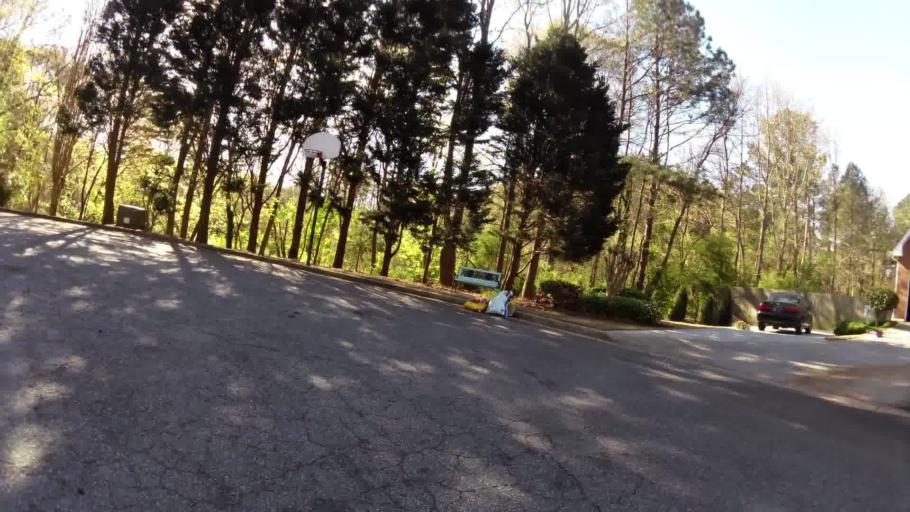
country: US
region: Georgia
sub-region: DeKalb County
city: Clarkston
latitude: 33.8310
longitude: -84.2684
